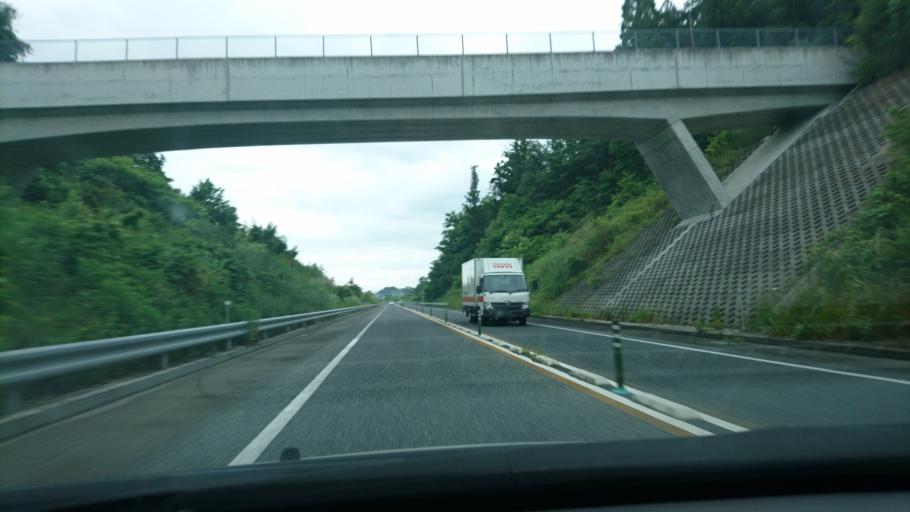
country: JP
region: Iwate
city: Ichinoseki
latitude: 38.7366
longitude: 141.1017
